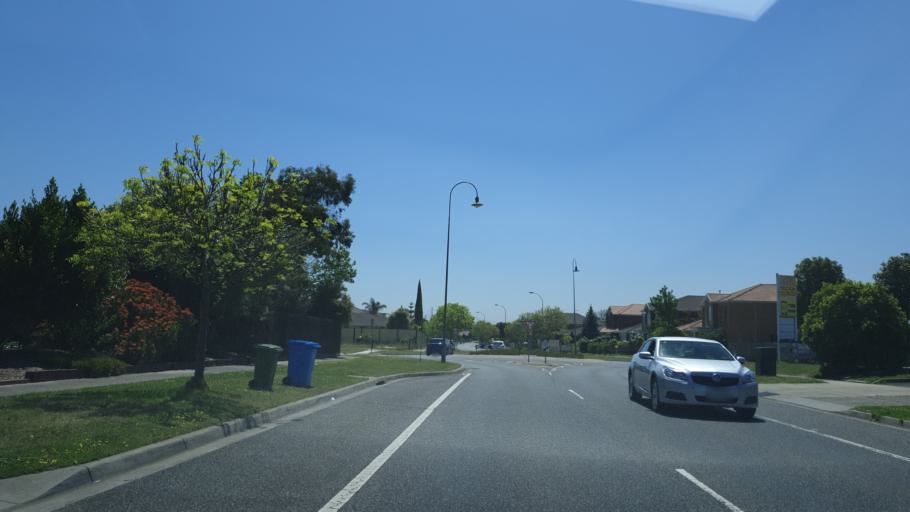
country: AU
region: Victoria
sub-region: Casey
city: Narre Warren South
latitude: -38.0575
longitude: 145.2899
